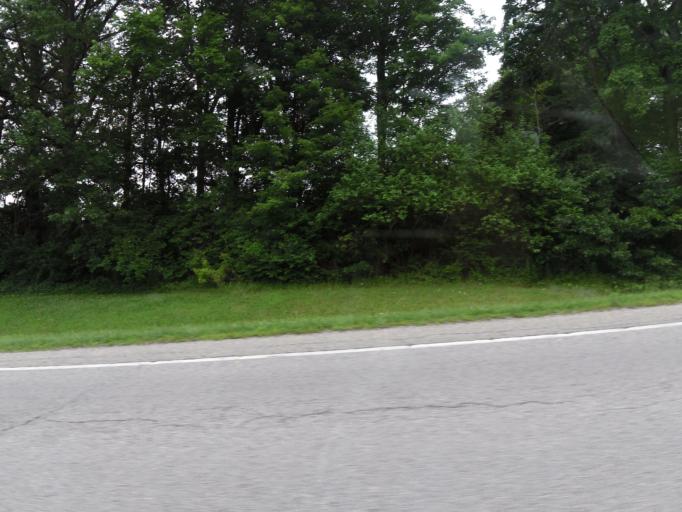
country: US
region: Ohio
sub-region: Brown County
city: Mount Orab
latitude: 39.0730
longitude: -83.9248
